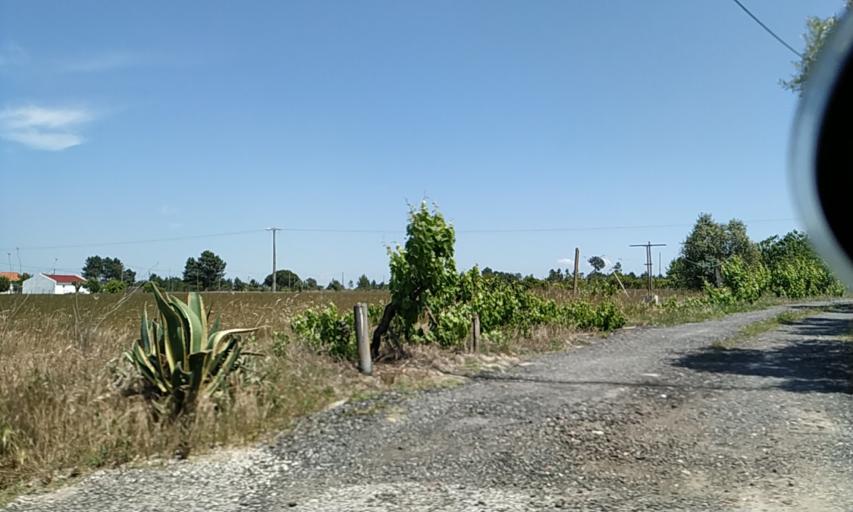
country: PT
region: Setubal
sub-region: Palmela
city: Pinhal Novo
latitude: 38.6550
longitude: -8.7416
